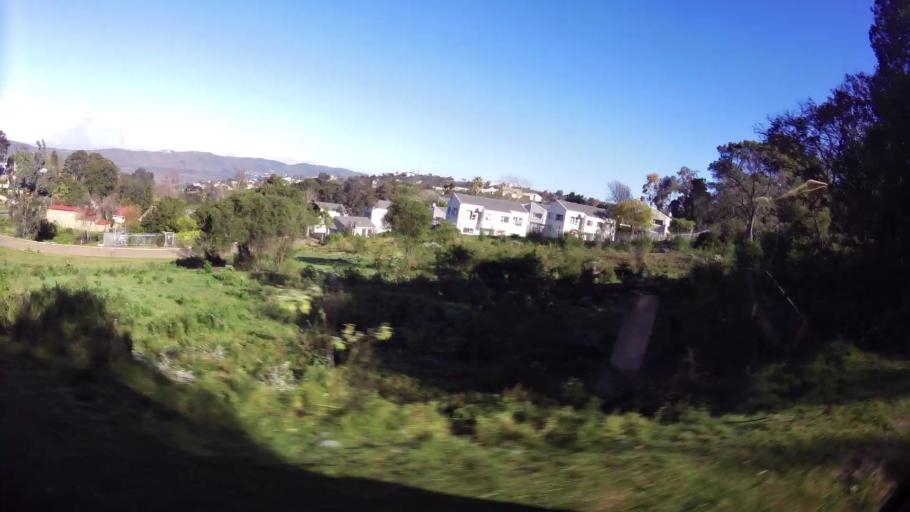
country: ZA
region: Western Cape
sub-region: Eden District Municipality
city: Knysna
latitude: -34.0286
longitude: 23.0516
